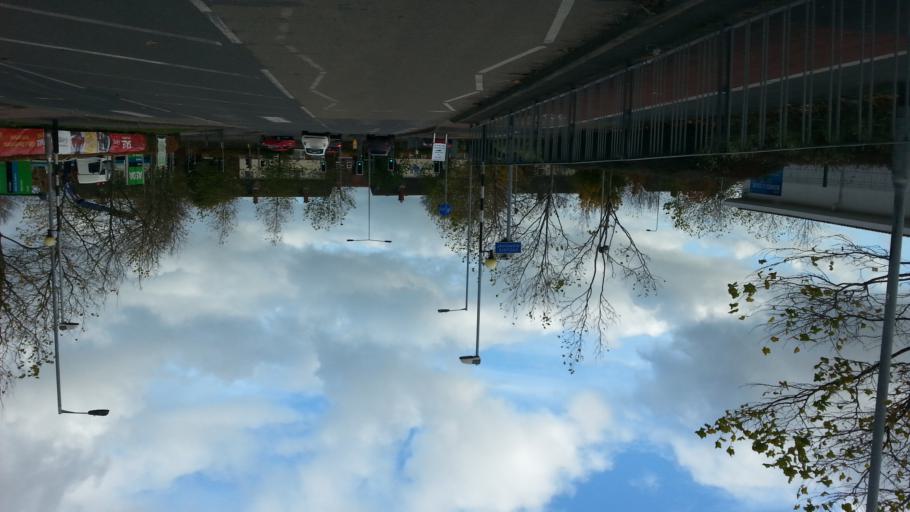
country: GB
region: England
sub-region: Staffordshire
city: Cannock
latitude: 52.6850
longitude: -2.0313
